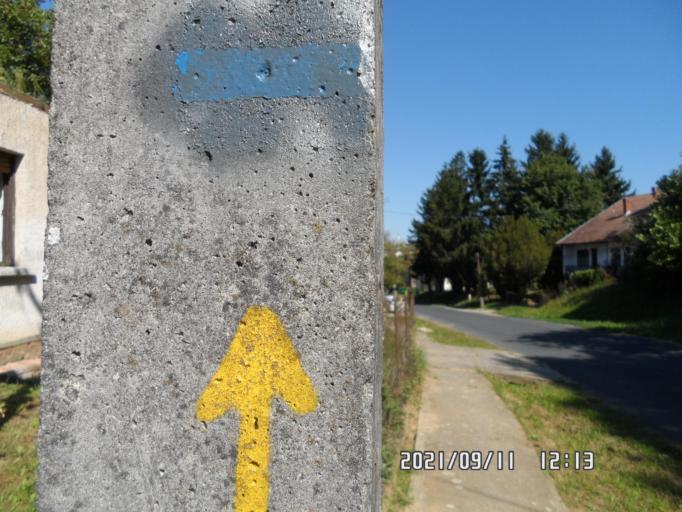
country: HU
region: Zala
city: Zalalovo
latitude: 46.7547
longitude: 16.6962
